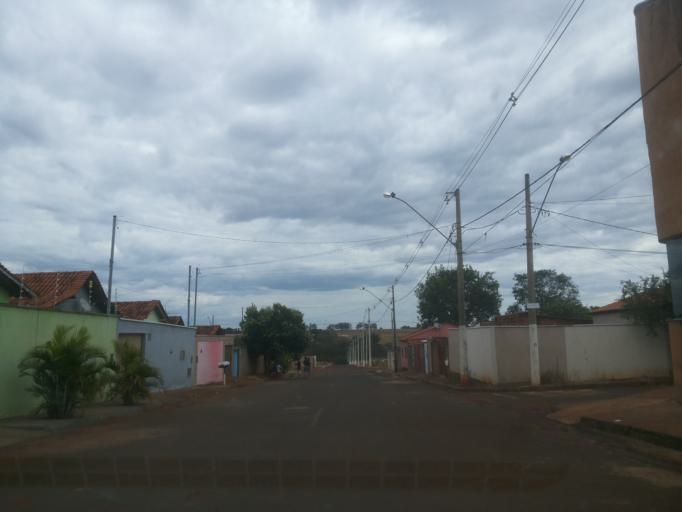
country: BR
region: Minas Gerais
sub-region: Centralina
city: Centralina
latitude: -18.7294
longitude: -49.2003
